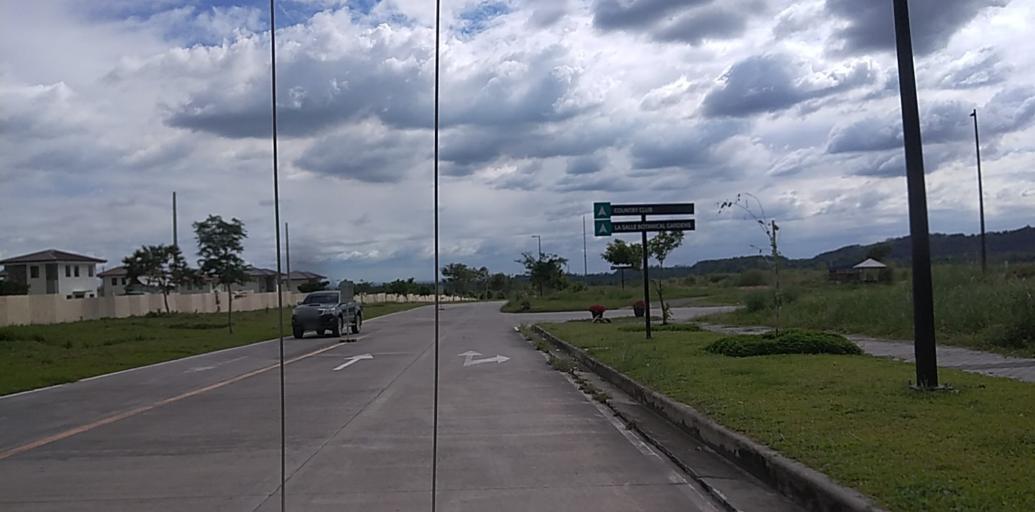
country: PH
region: Central Luzon
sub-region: Province of Pampanga
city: Dolores
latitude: 15.1142
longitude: 120.5128
